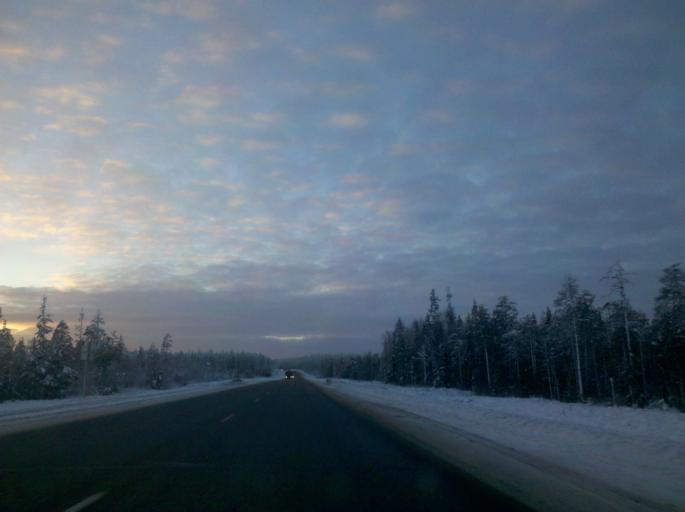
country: RU
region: Republic of Karelia
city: Medvezh'yegorsk
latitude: 62.8219
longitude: 34.2280
